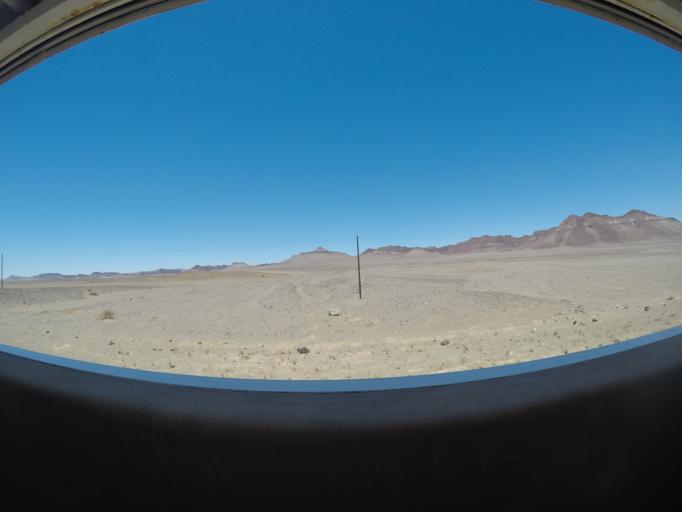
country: ZA
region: Northern Cape
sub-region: Namakwa District Municipality
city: Port Nolloth
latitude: -28.6029
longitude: 17.4858
